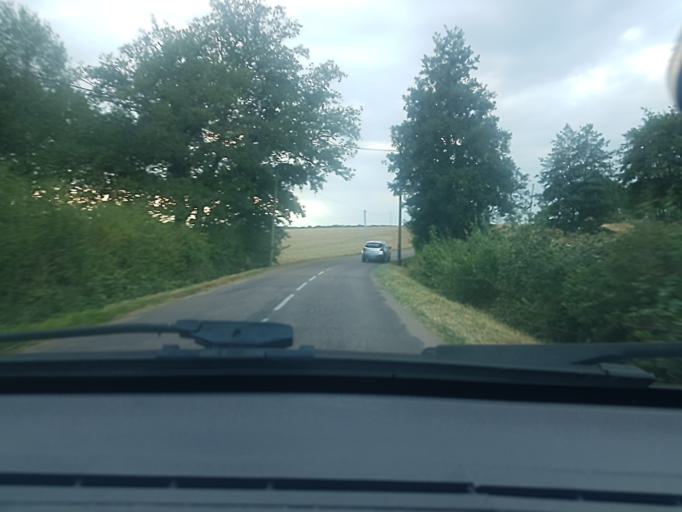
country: FR
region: Bourgogne
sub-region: Departement de Saone-et-Loire
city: Buxy
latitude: 46.7016
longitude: 4.7741
